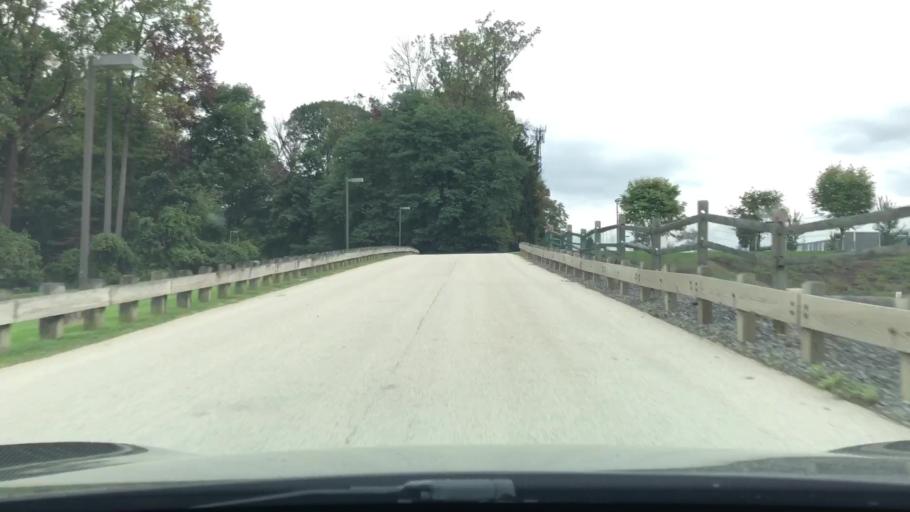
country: US
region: Pennsylvania
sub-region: Chester County
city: Berwyn
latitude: 39.9902
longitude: -75.4156
